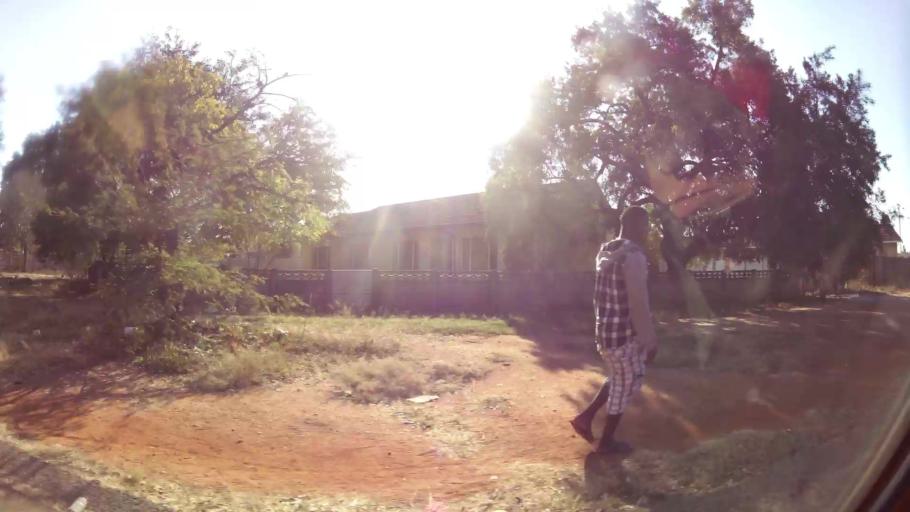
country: ZA
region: North-West
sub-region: Bojanala Platinum District Municipality
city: Rustenburg
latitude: -25.6520
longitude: 27.2396
